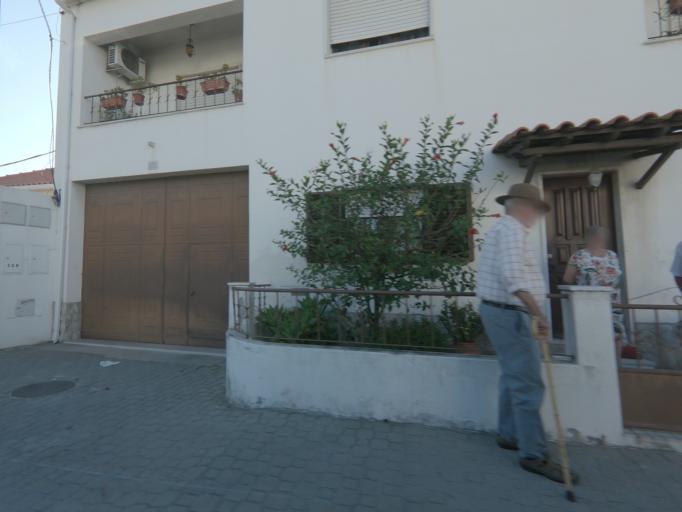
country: PT
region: Setubal
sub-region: Palmela
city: Quinta do Anjo
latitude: 38.5306
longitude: -8.9908
